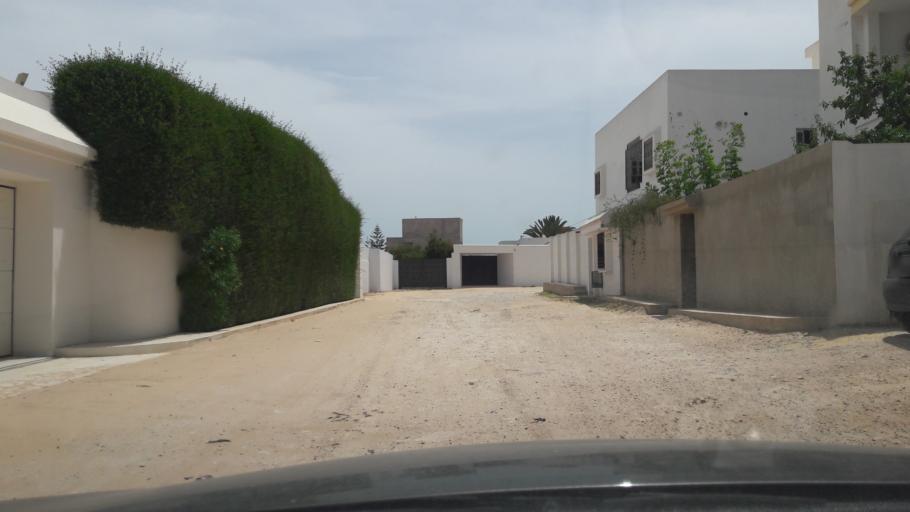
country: TN
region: Safaqis
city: Al Qarmadah
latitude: 34.7816
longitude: 10.7581
